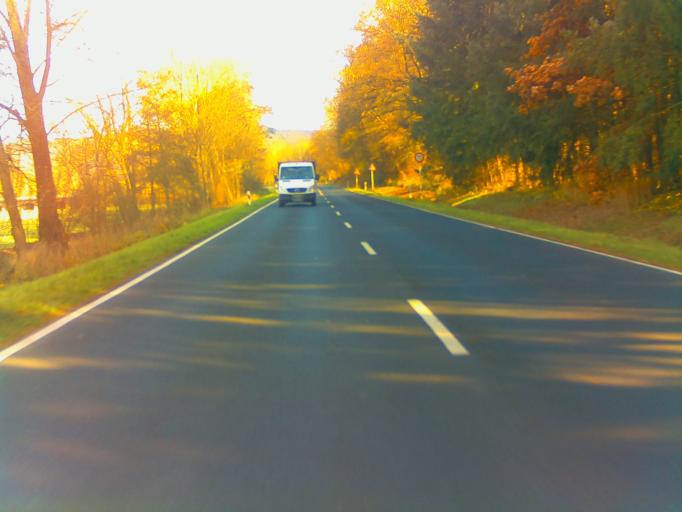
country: DE
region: Bavaria
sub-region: Regierungsbezirk Unterfranken
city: Bad Kissingen
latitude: 50.2329
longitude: 10.0709
